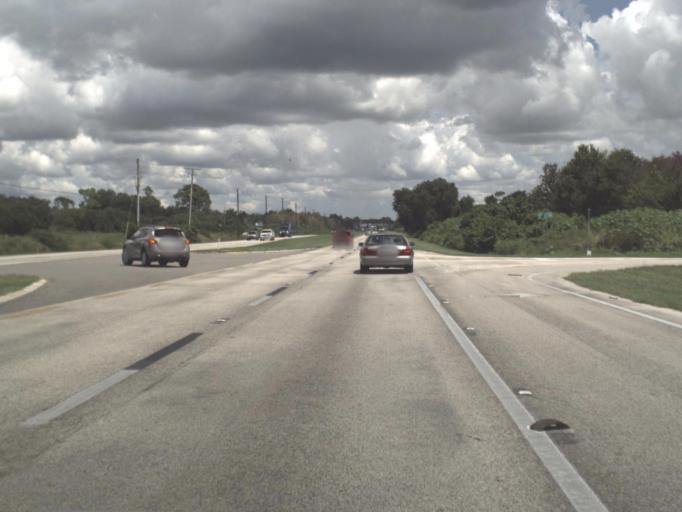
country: US
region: Florida
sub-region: Polk County
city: Lake Alfred
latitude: 28.0697
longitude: -81.7465
